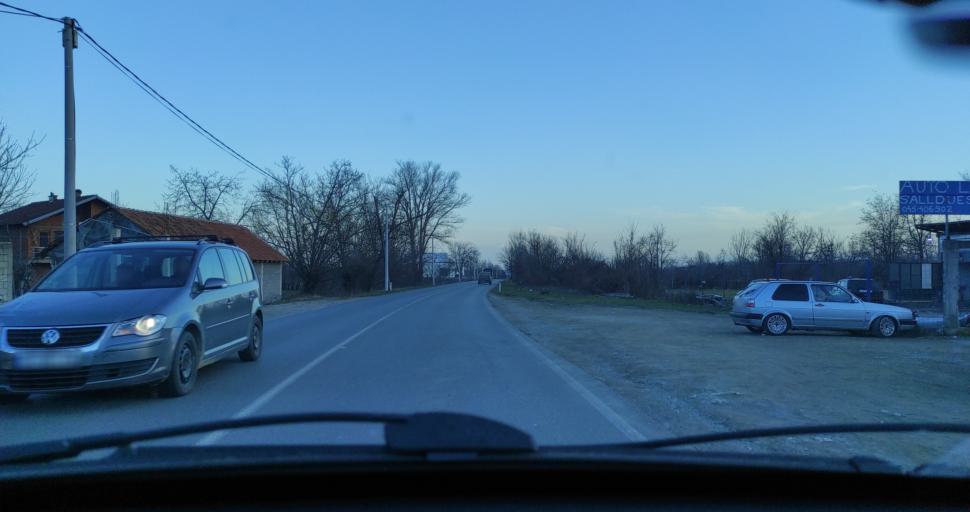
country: XK
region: Gjakova
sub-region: Komuna e Decanit
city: Dranoc
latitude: 42.5221
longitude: 20.3035
